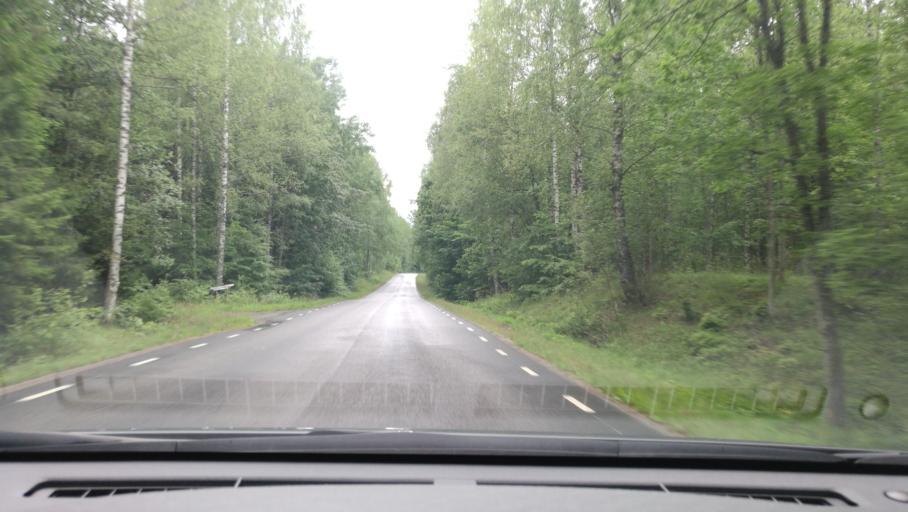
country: SE
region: OEstergoetland
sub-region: Norrkopings Kommun
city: Svartinge
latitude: 58.8237
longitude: 15.9786
